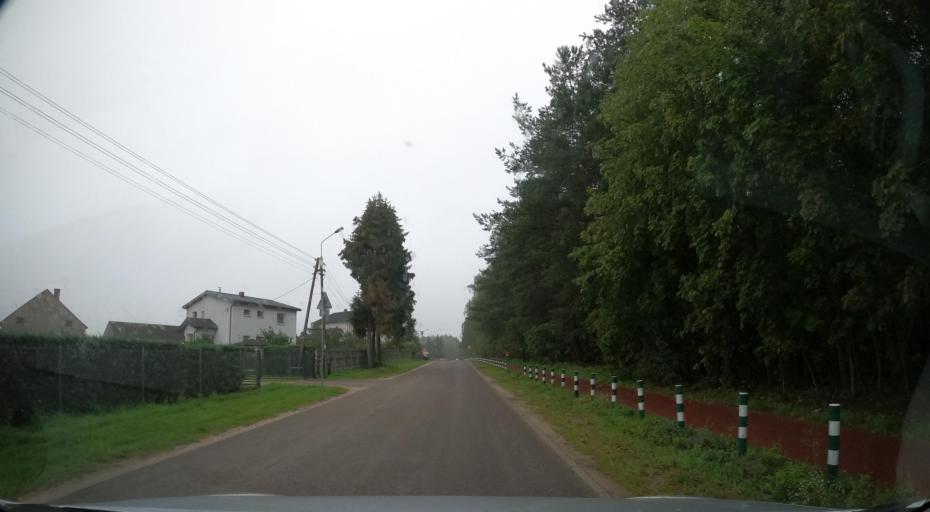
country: PL
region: Pomeranian Voivodeship
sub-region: Powiat kartuski
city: Chwaszczyno
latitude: 54.4378
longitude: 18.4183
